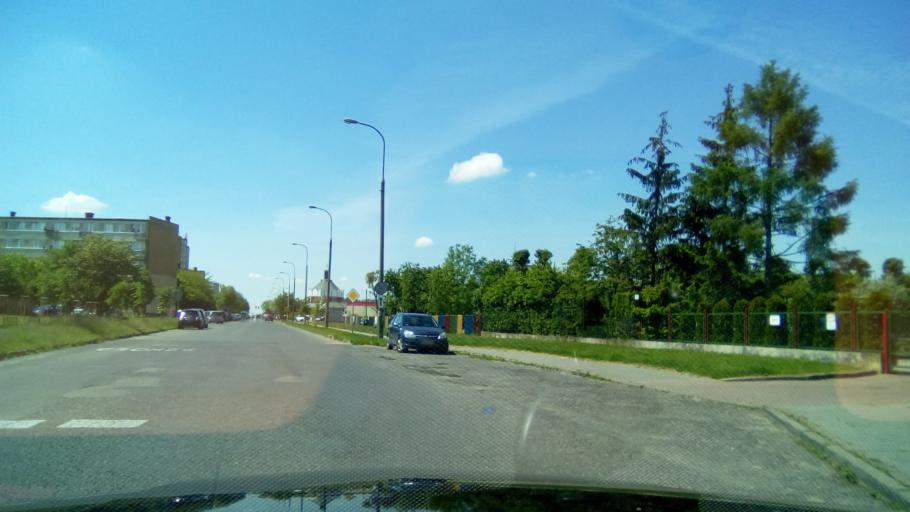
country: PL
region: Greater Poland Voivodeship
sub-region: Powiat gnieznienski
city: Gniezno
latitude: 52.5491
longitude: 17.6103
